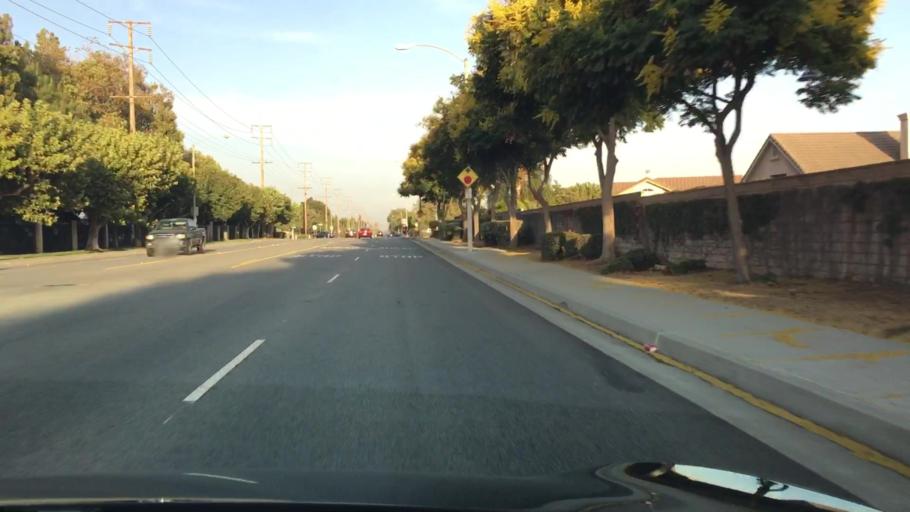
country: US
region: California
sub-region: San Bernardino County
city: Ontario
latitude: 34.0266
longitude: -117.6434
